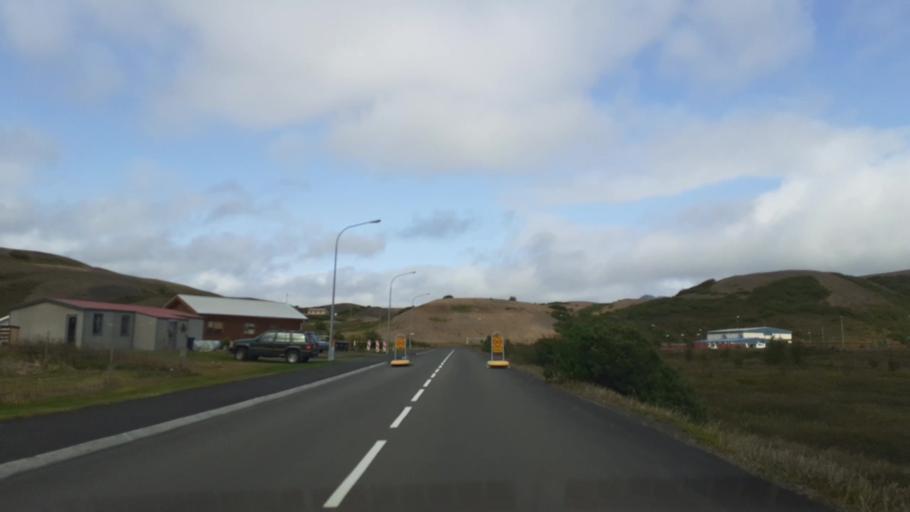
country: IS
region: Northeast
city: Laugar
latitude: 65.6407
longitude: -16.8957
